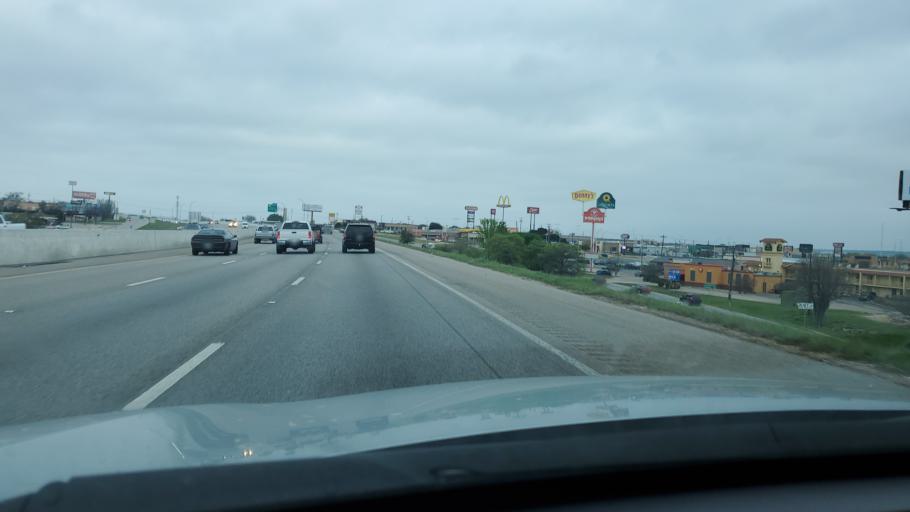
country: US
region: Texas
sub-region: Bell County
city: Killeen
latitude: 31.1079
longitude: -97.7457
